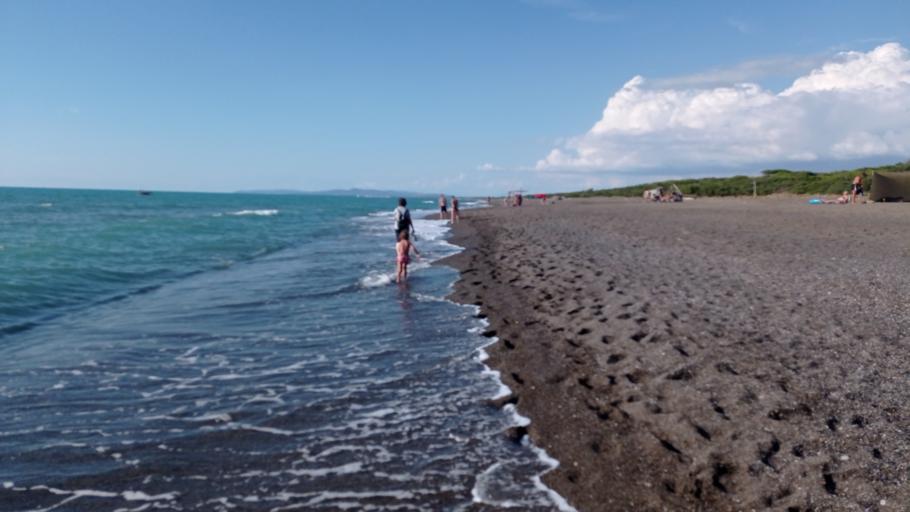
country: IT
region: Tuscany
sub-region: Provincia di Livorno
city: Donoratico
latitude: 43.1950
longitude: 10.5353
